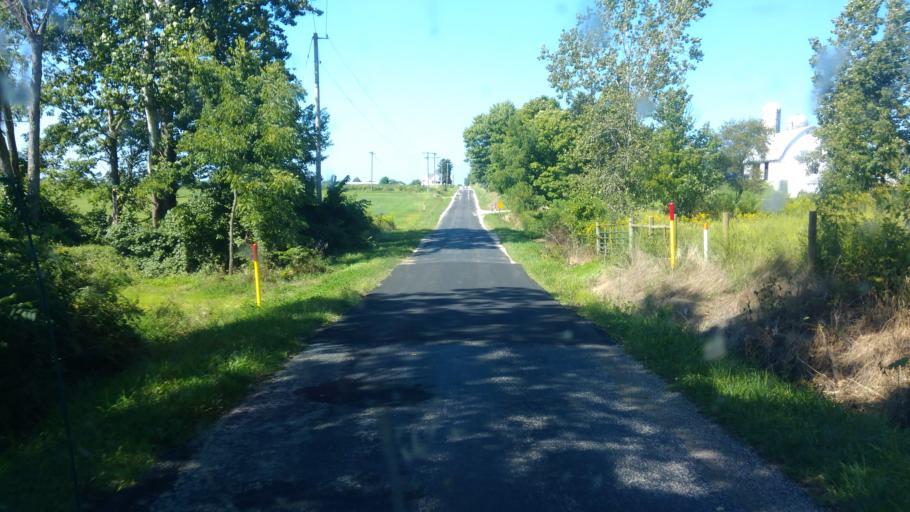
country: US
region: Ohio
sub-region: Ashland County
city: Ashland
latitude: 40.9232
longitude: -82.2625
